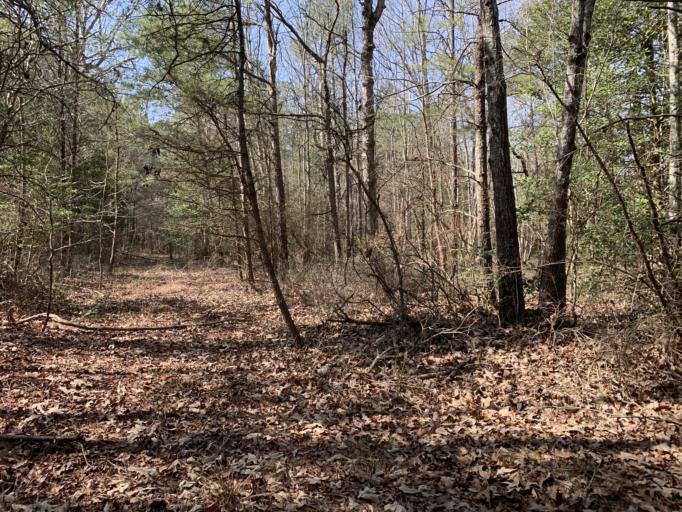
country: US
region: Delaware
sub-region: Sussex County
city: Georgetown
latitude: 38.6838
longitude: -75.4731
